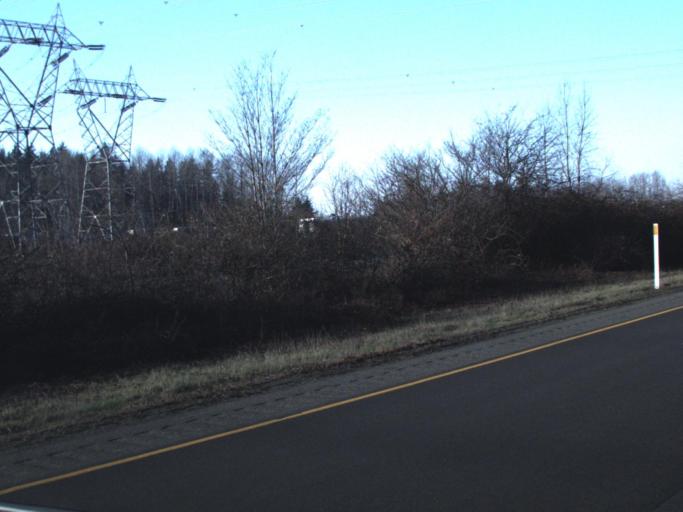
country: US
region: Washington
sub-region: Whatcom County
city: Ferndale
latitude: 48.9069
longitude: -122.6207
